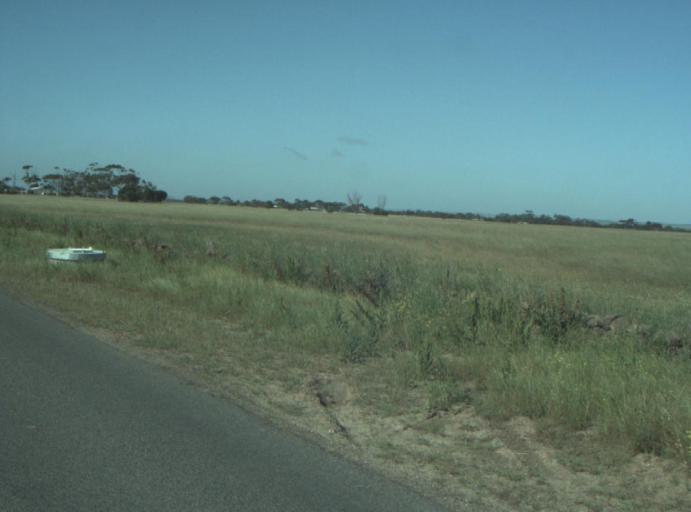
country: AU
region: Victoria
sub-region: Wyndham
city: Little River
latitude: -37.9600
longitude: 144.4635
